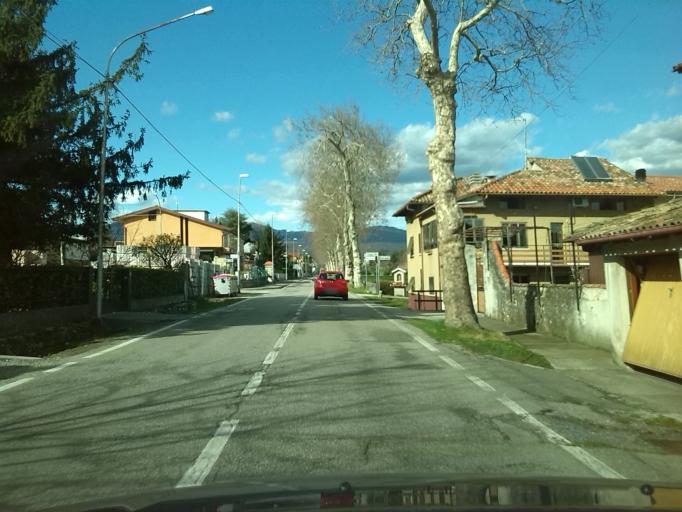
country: IT
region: Friuli Venezia Giulia
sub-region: Provincia di Udine
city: Cividale del Friuli
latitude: 46.0804
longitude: 13.4358
